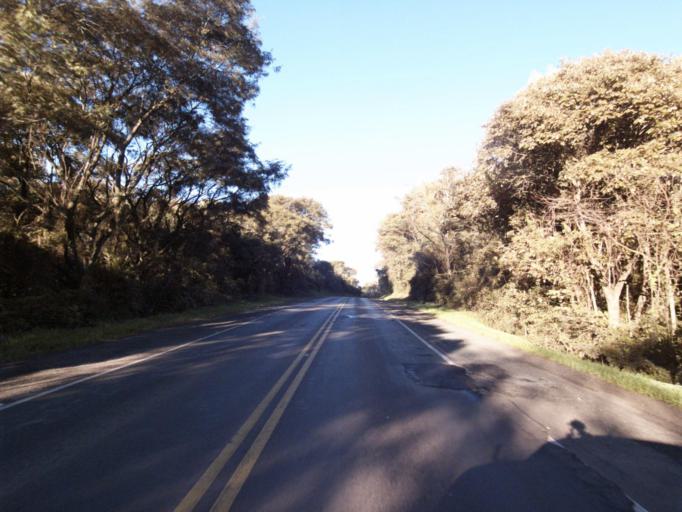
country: BR
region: Santa Catarina
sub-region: Sao Lourenco Do Oeste
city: Sao Lourenco dOeste
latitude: -26.7722
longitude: -53.2700
